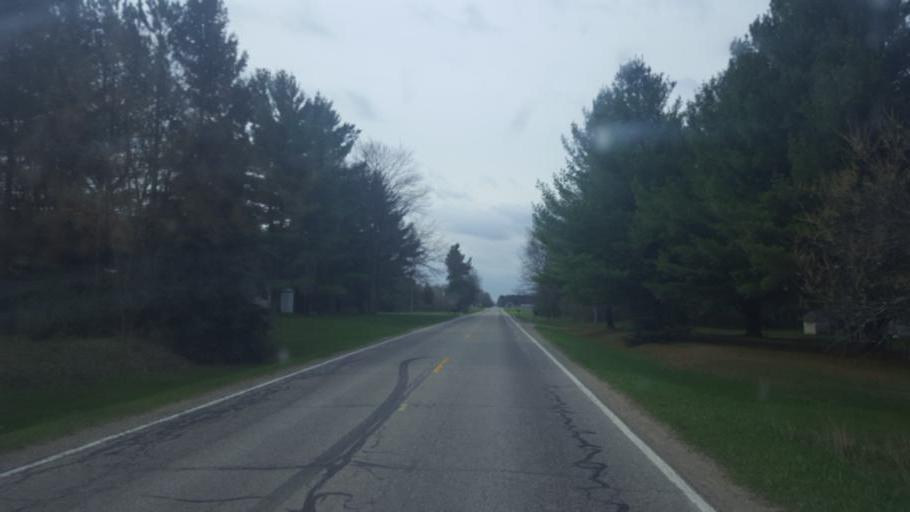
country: US
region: Michigan
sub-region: Isabella County
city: Lake Isabella
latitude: 43.5417
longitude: -84.9865
